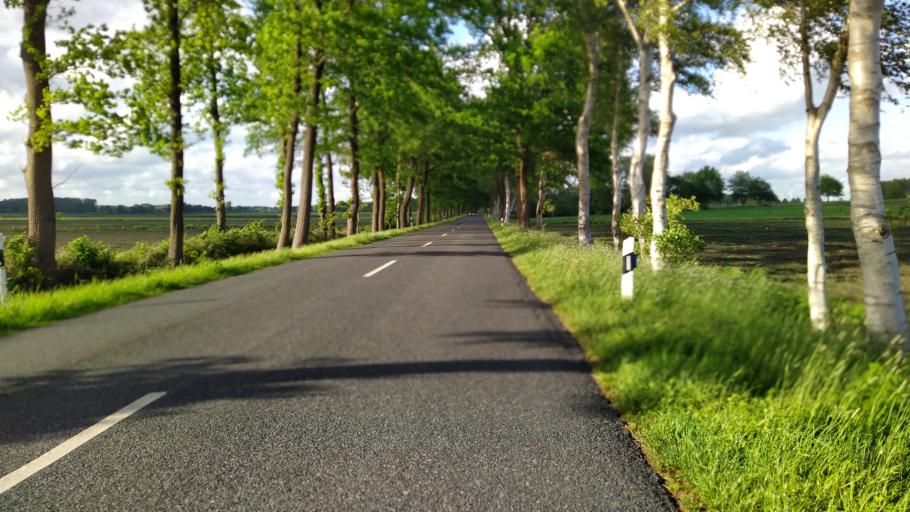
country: DE
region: Lower Saxony
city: Farven
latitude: 53.4532
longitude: 9.2783
